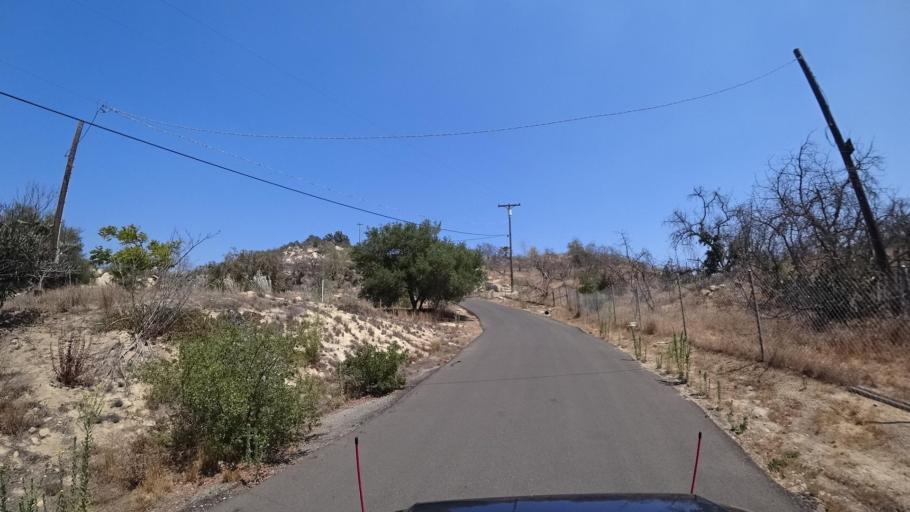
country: US
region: California
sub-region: San Diego County
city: Fallbrook
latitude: 33.4373
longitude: -117.3022
